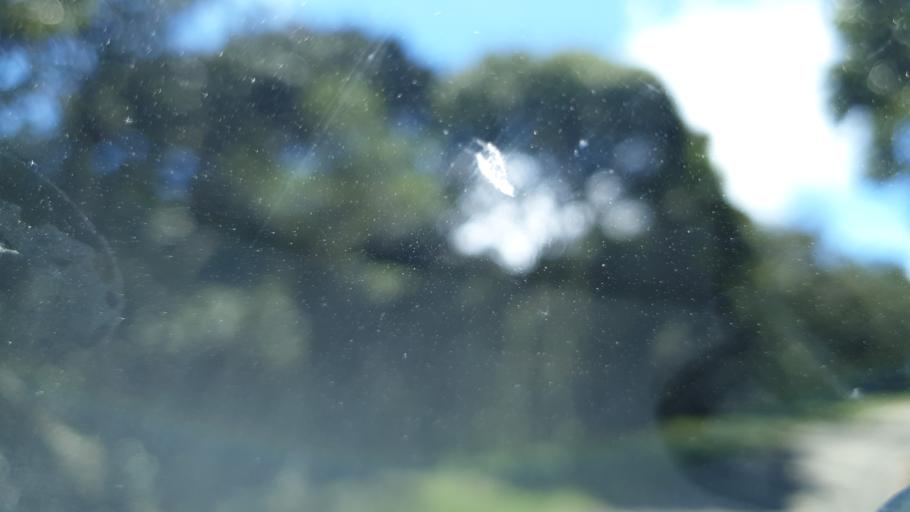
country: LK
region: Uva
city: Haputale
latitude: 6.8008
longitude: 80.8343
